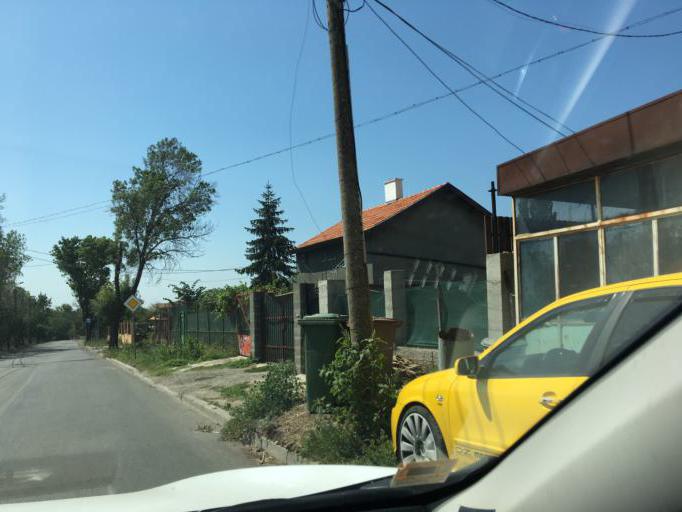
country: BG
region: Burgas
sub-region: Obshtina Kameno
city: Kameno
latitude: 42.6228
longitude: 27.3954
